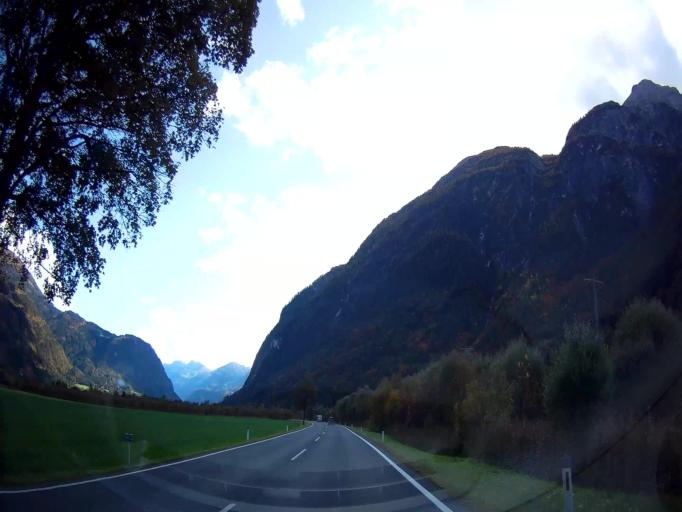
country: AT
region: Tyrol
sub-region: Politischer Bezirk Lienz
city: Nikolsdorf
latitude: 46.7883
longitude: 12.8783
